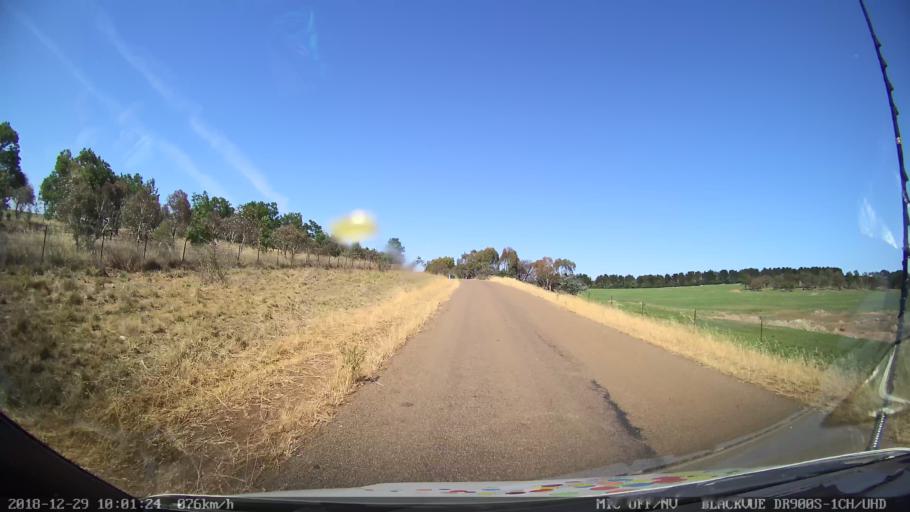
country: AU
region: New South Wales
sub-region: Goulburn Mulwaree
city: Goulburn
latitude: -34.7987
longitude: 149.4766
